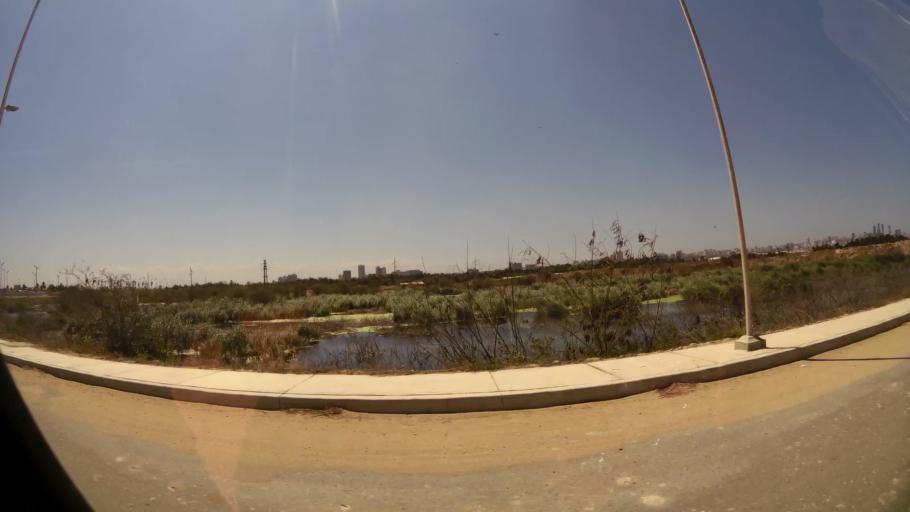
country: CO
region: Atlantico
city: Barranquilla
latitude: 10.9949
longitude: -74.7701
